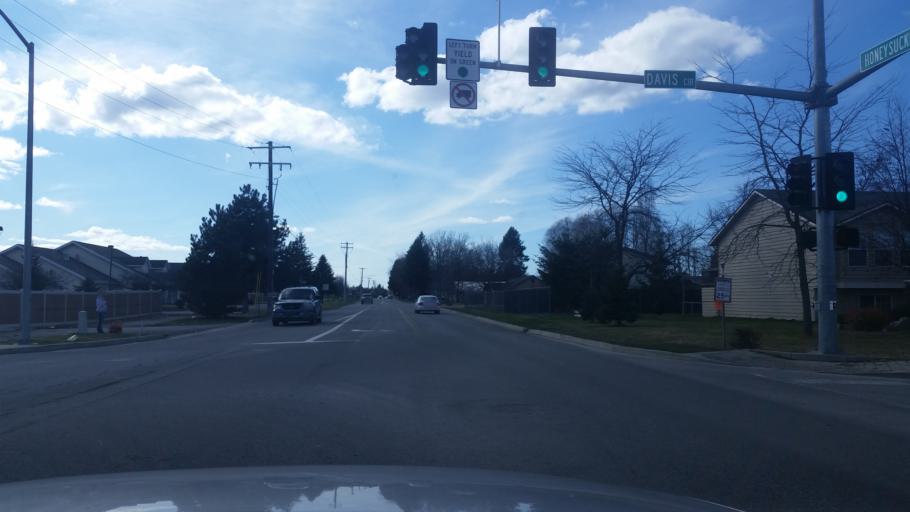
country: US
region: Idaho
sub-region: Kootenai County
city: Hayden
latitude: 47.7518
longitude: -116.7941
